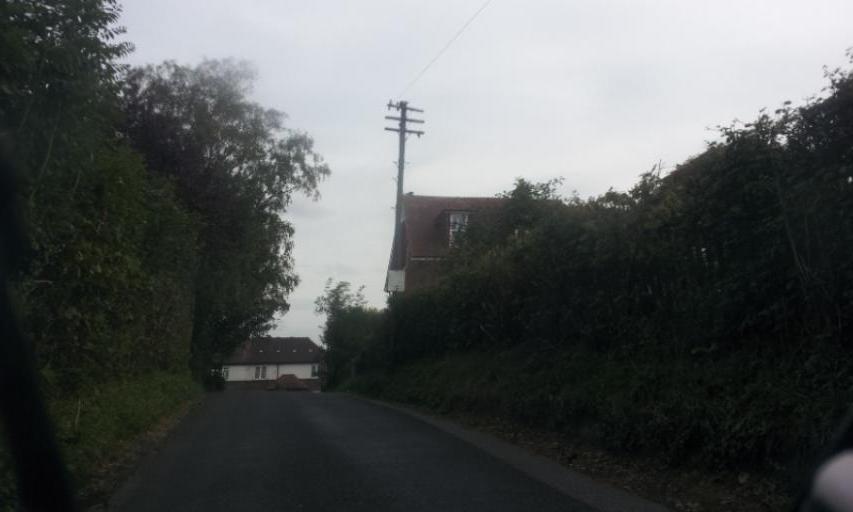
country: GB
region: England
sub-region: Kent
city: Tonbridge
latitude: 51.1702
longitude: 0.2371
